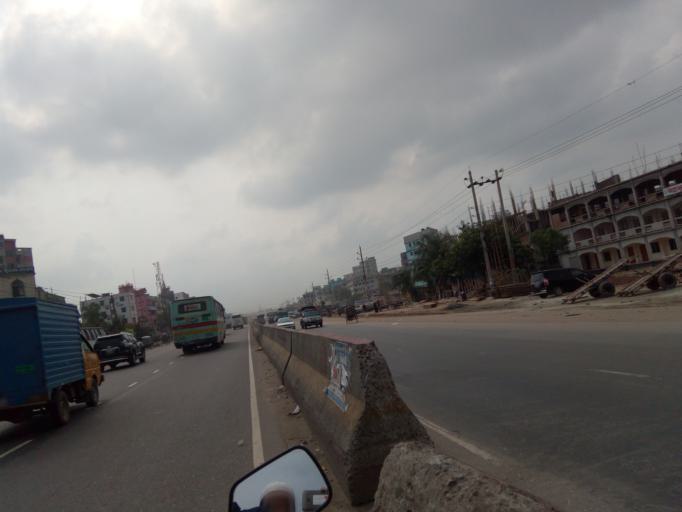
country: BD
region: Dhaka
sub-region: Dhaka
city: Dhaka
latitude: 23.7044
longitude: 90.4469
